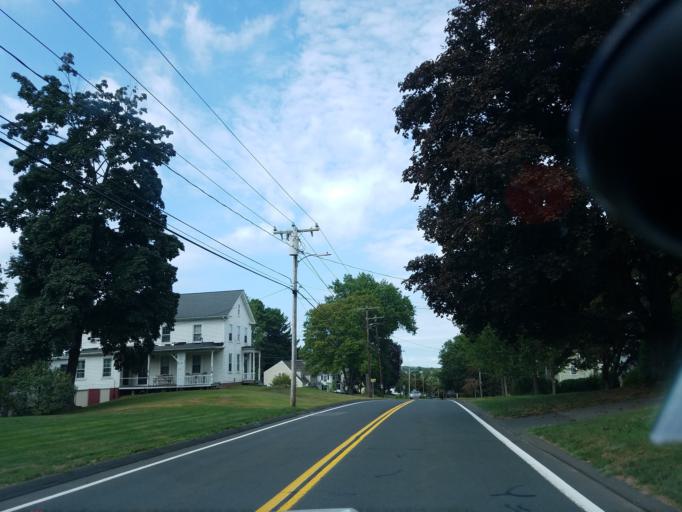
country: US
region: Connecticut
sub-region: Hartford County
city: Wethersfield
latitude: 41.6791
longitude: -72.6464
